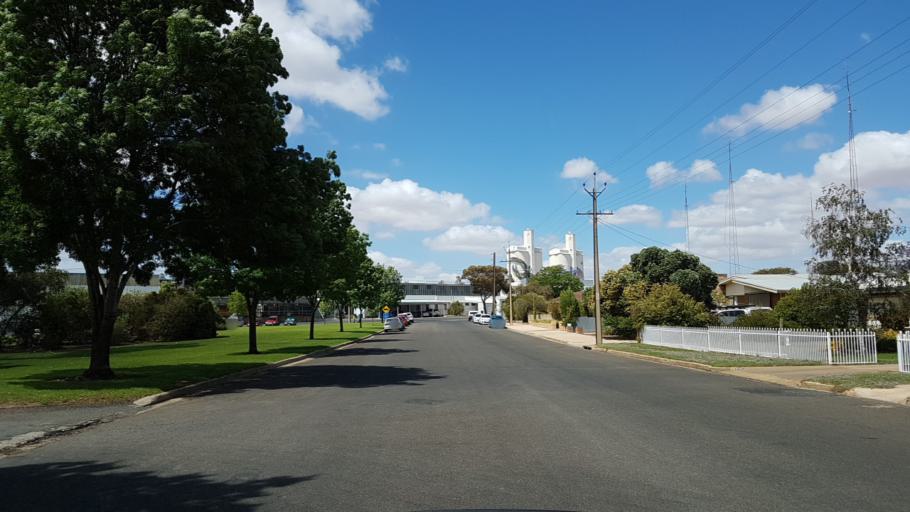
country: AU
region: South Australia
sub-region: Loxton Waikerie
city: Waikerie
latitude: -34.1827
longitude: 139.9874
